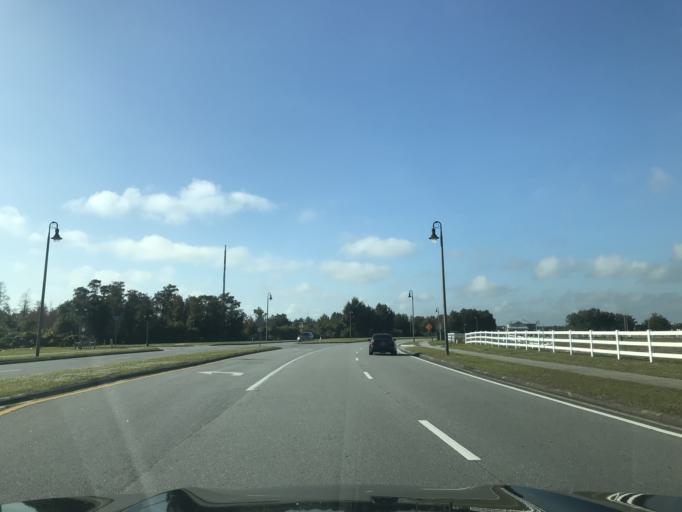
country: US
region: Florida
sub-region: Polk County
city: Citrus Ridge
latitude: 28.3378
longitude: -81.6015
